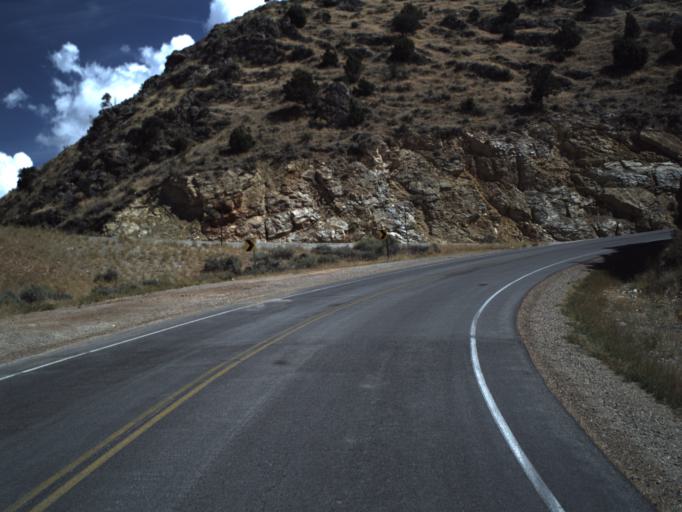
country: US
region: Utah
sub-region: Rich County
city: Randolph
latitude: 41.8248
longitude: -111.2939
